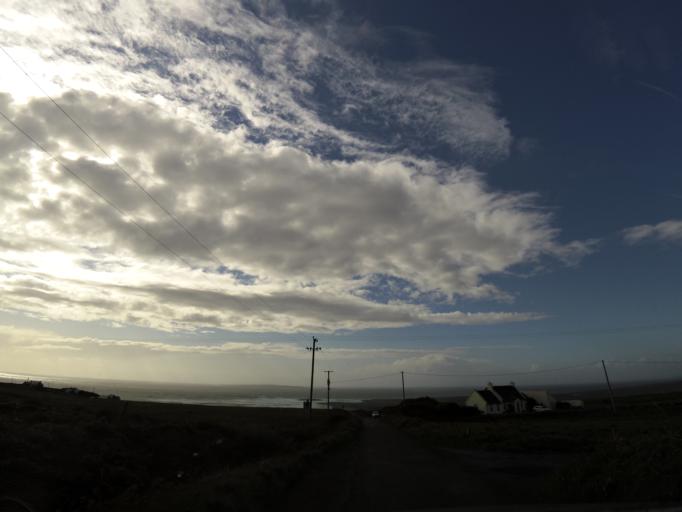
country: IE
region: Connaught
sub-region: County Galway
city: Bearna
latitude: 53.0015
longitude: -9.3827
